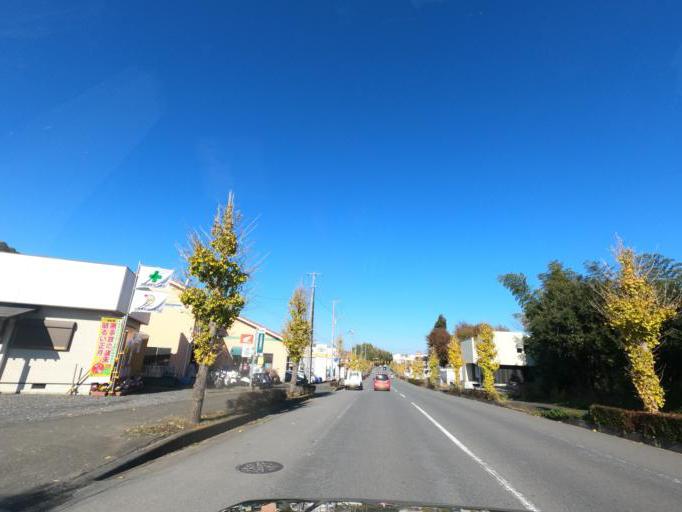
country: JP
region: Ibaraki
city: Mitsukaido
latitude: 35.9844
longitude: 139.9772
